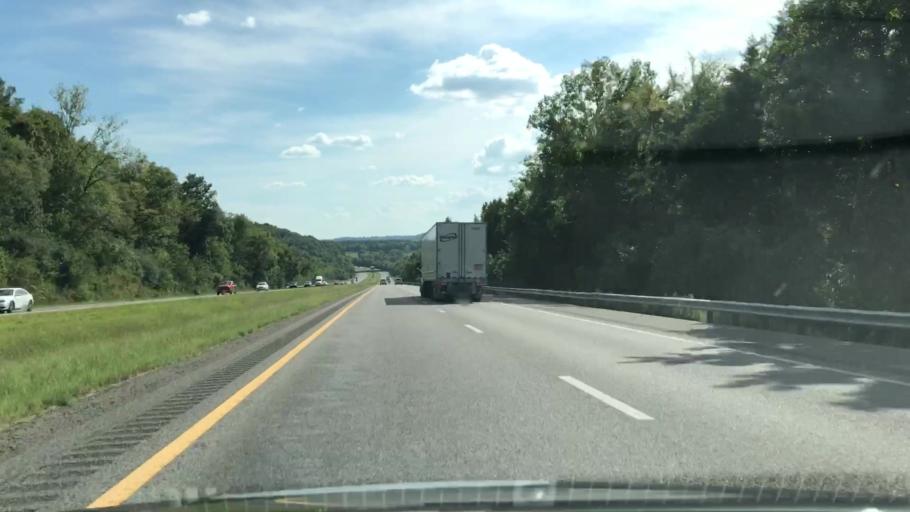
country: US
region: Alabama
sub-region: Limestone County
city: Ardmore
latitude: 35.1162
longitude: -86.8803
